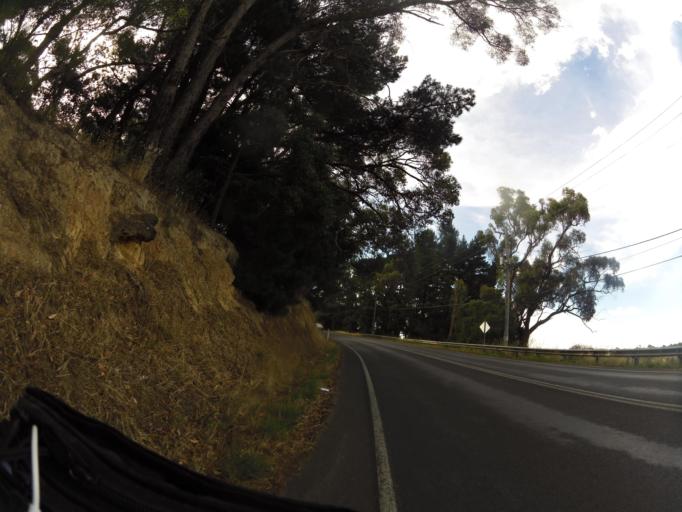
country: AU
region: Victoria
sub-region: Ballarat North
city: Mount Clear
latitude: -37.6144
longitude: 143.8735
